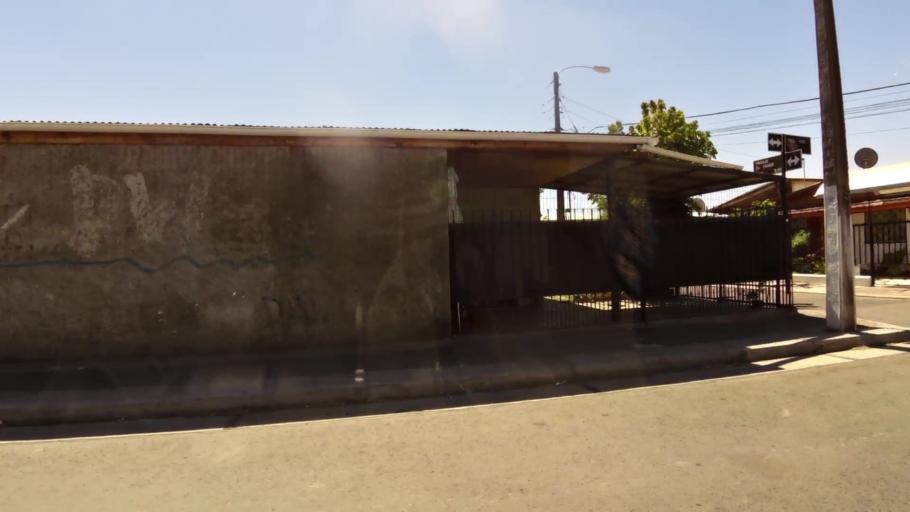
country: CL
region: O'Higgins
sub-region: Provincia de Cachapoal
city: Rancagua
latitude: -34.1712
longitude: -70.7651
